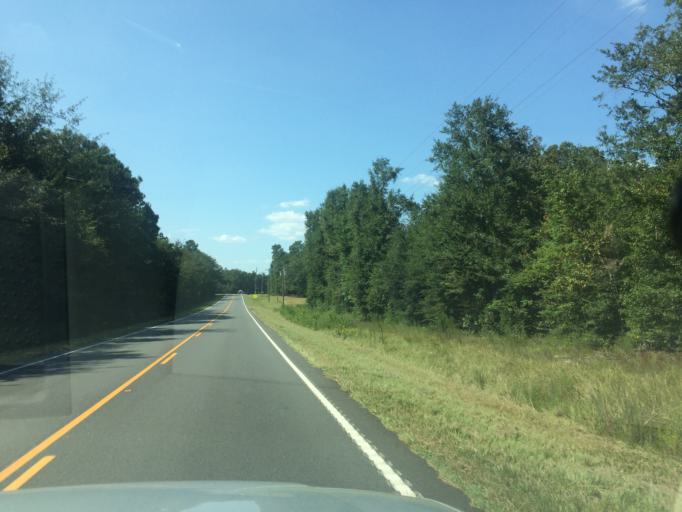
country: US
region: South Carolina
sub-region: Lexington County
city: Batesburg-Leesville
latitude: 33.7087
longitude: -81.4913
